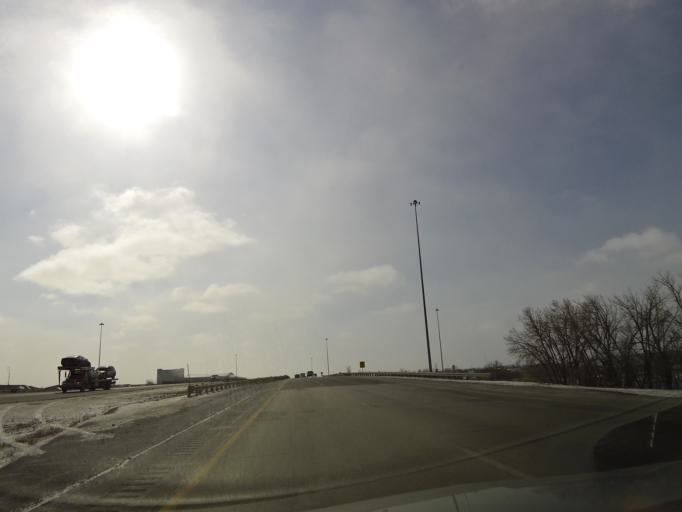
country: US
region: North Dakota
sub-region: Grand Forks County
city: Grand Forks
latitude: 47.9201
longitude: -97.0937
